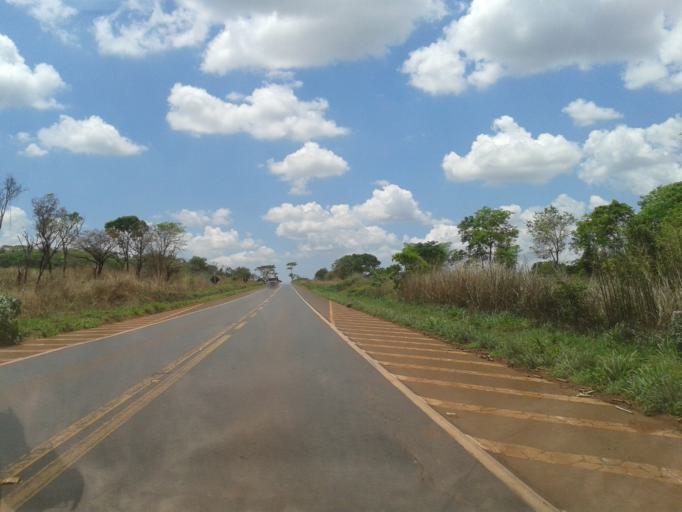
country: BR
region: Goias
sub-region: Itumbiara
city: Itumbiara
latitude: -18.3488
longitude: -49.3922
